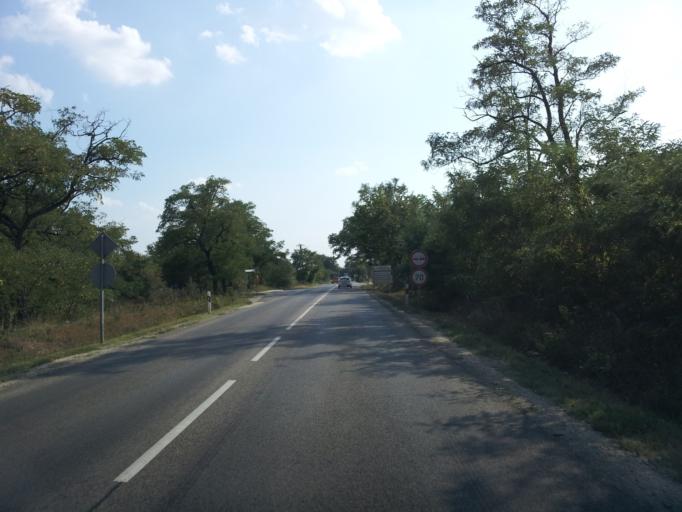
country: HU
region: Pest
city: Szigethalom
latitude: 47.3028
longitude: 19.0338
